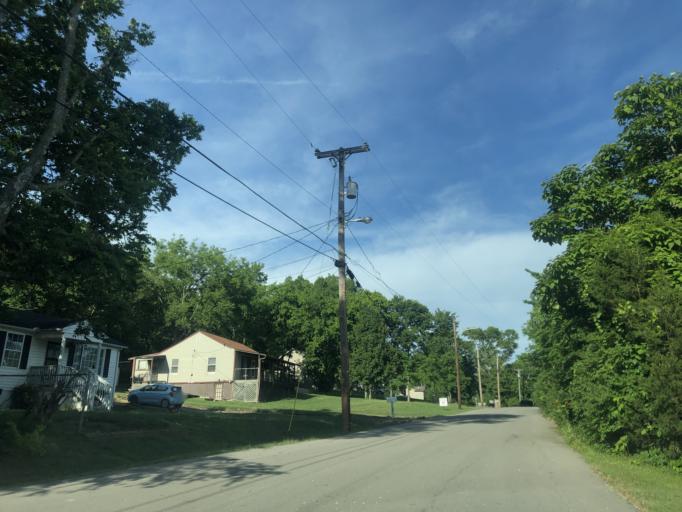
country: US
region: Tennessee
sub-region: Davidson County
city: Nashville
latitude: 36.2199
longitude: -86.8356
